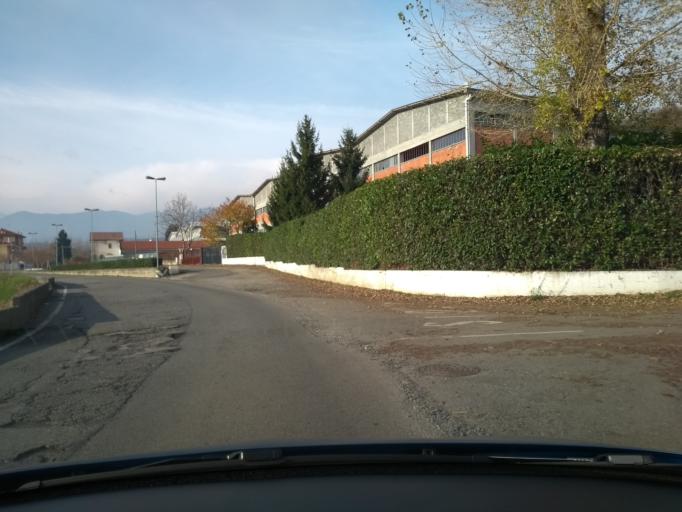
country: IT
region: Piedmont
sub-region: Provincia di Torino
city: Balangero
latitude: 45.2676
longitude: 7.5306
